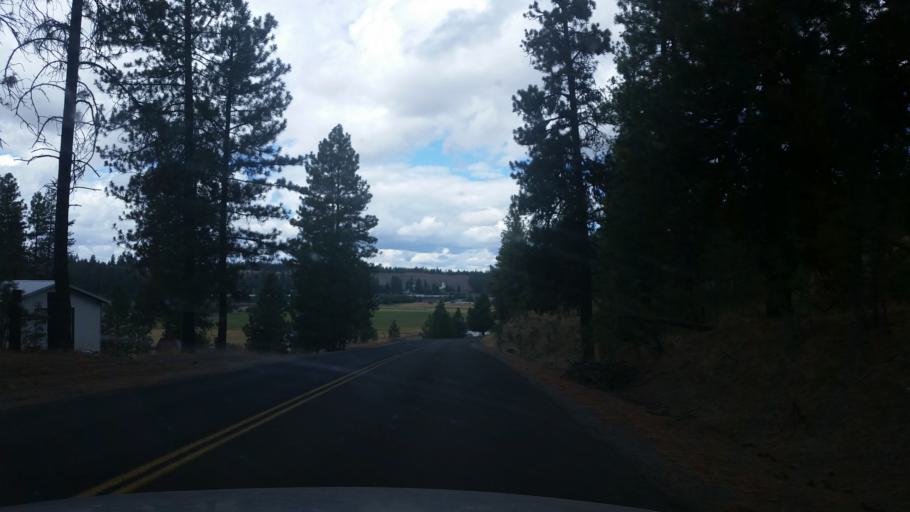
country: US
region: Washington
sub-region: Spokane County
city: Cheney
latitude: 47.5552
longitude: -117.4870
